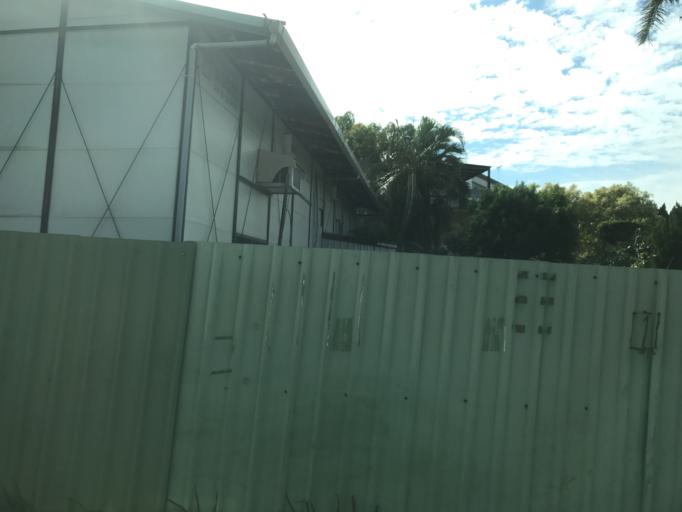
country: TW
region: Taiwan
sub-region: Hsinchu
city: Hsinchu
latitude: 24.7805
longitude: 120.9346
